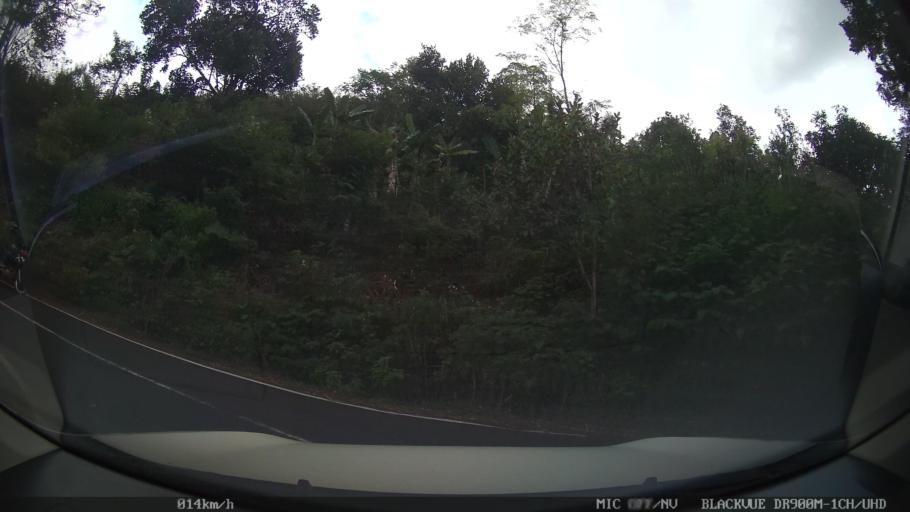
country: ID
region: Bali
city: Banjar Kedisan
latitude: -8.2595
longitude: 115.3475
